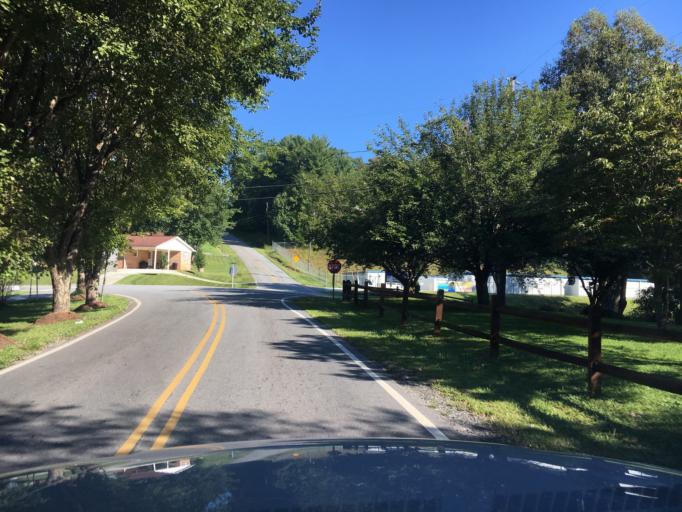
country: US
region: North Carolina
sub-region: McDowell County
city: West Marion
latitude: 35.6652
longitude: -82.0365
